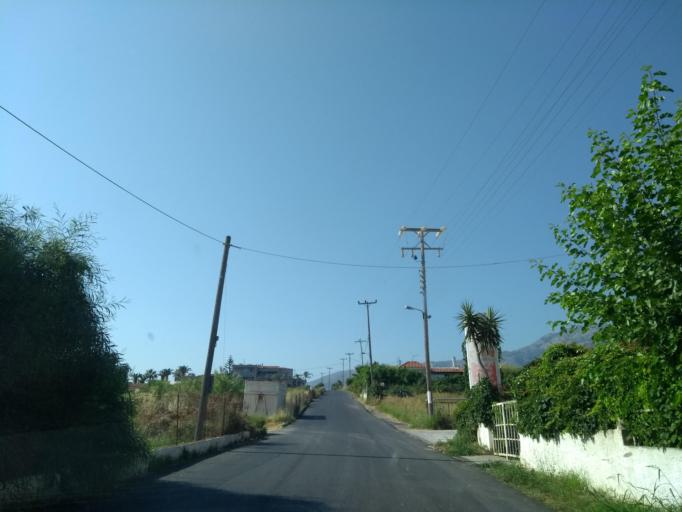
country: GR
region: Crete
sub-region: Nomos Chanias
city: Georgioupolis
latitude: 35.3477
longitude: 24.2979
